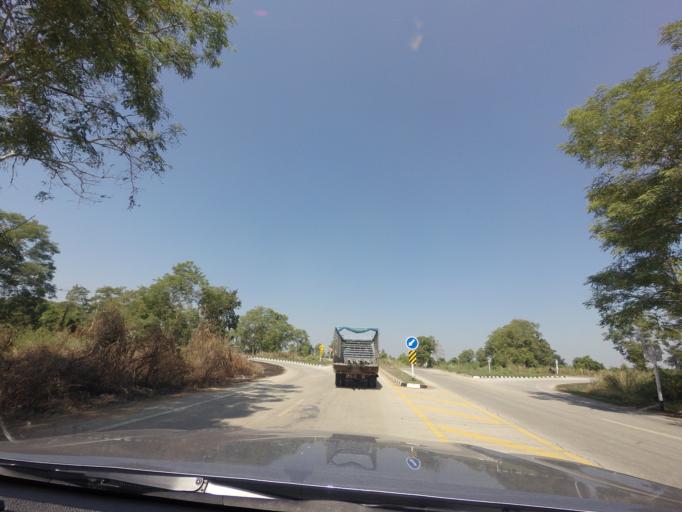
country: TH
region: Sukhothai
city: Si Samrong
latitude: 17.1116
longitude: 99.7772
